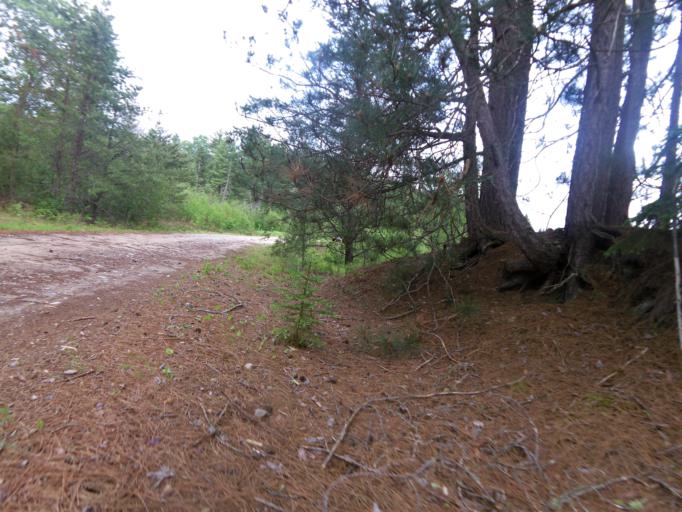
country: CA
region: Quebec
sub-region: Outaouais
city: Shawville
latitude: 45.9114
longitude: -76.2993
